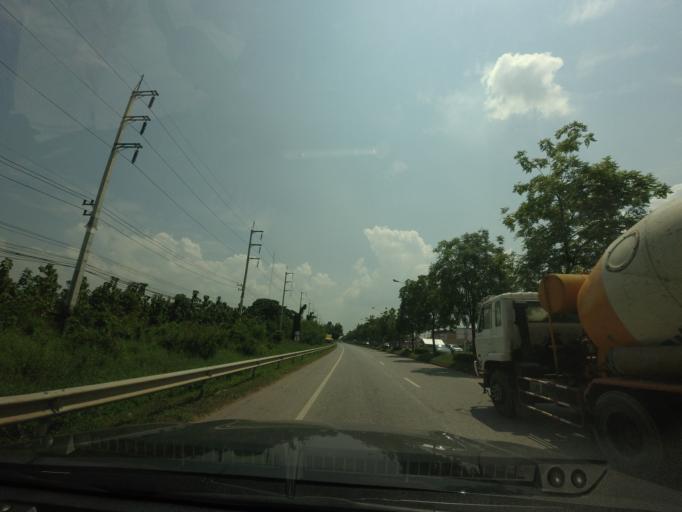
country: TH
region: Uttaradit
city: Uttaradit
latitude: 17.5969
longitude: 100.1276
